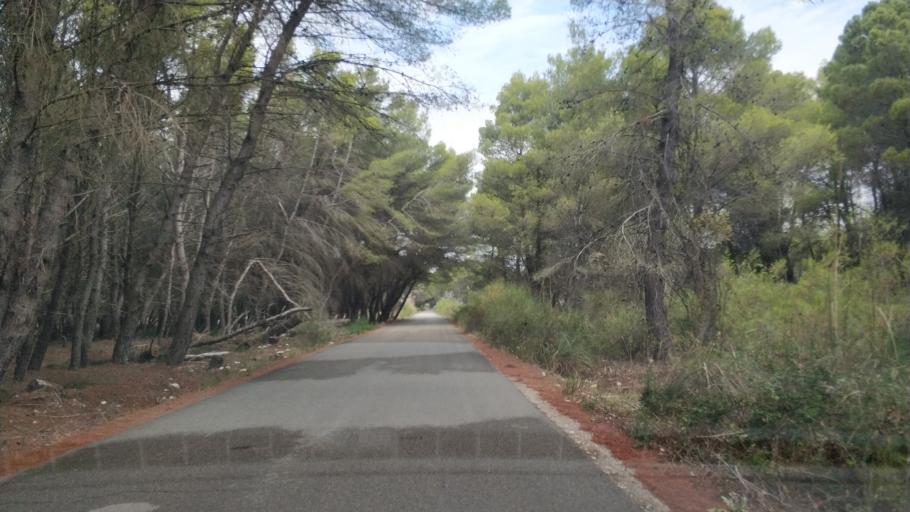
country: AL
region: Vlore
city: Vlore
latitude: 40.4931
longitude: 19.4354
